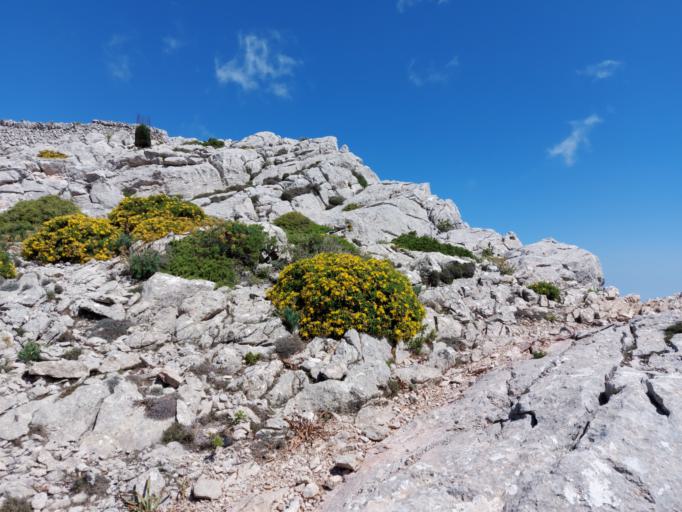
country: ES
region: Balearic Islands
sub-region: Illes Balears
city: Escorca
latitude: 39.8091
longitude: 2.8523
